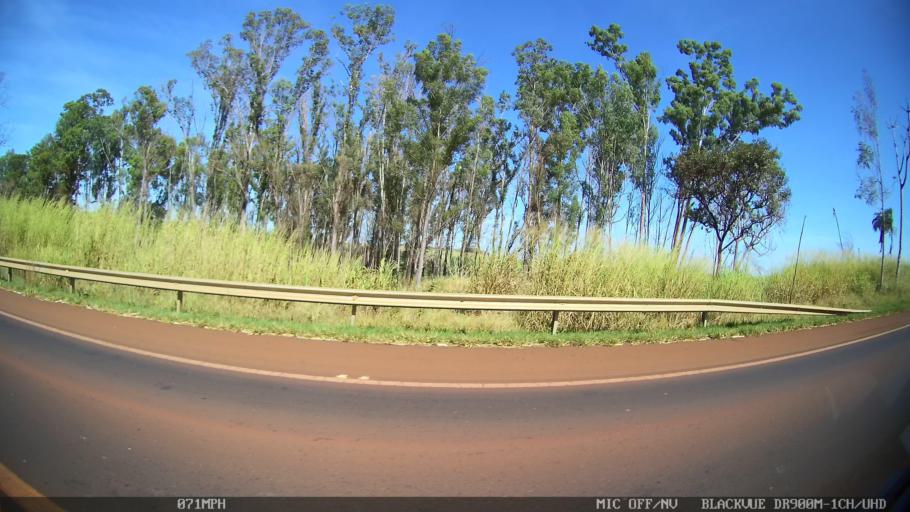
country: BR
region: Sao Paulo
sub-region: Sao Joaquim Da Barra
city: Sao Joaquim da Barra
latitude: -20.5466
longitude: -47.7708
